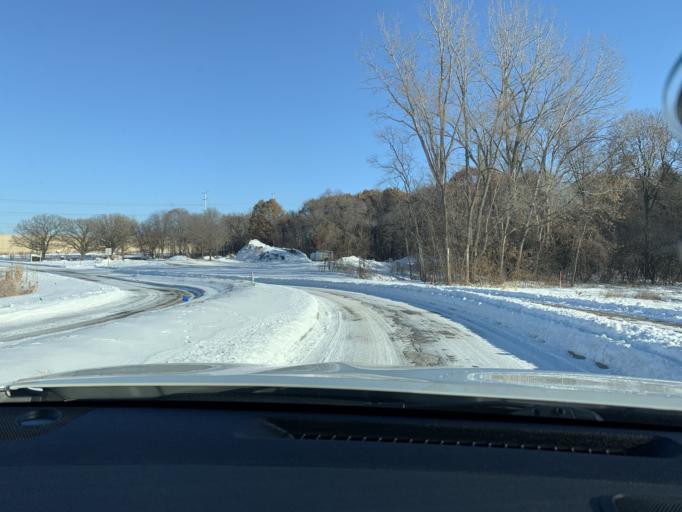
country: US
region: Minnesota
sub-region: Anoka County
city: Fridley
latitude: 45.0945
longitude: -93.2584
